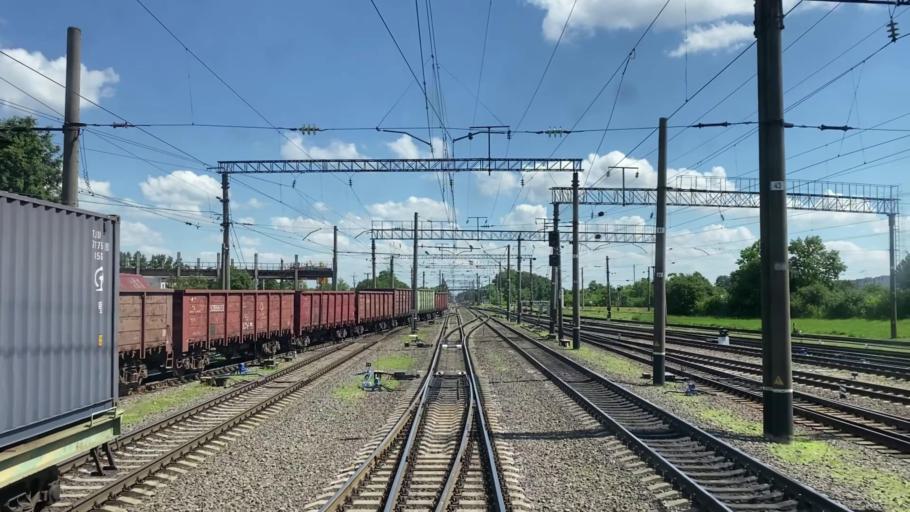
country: BY
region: Brest
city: Baranovichi
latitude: 53.1432
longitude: 26.0207
